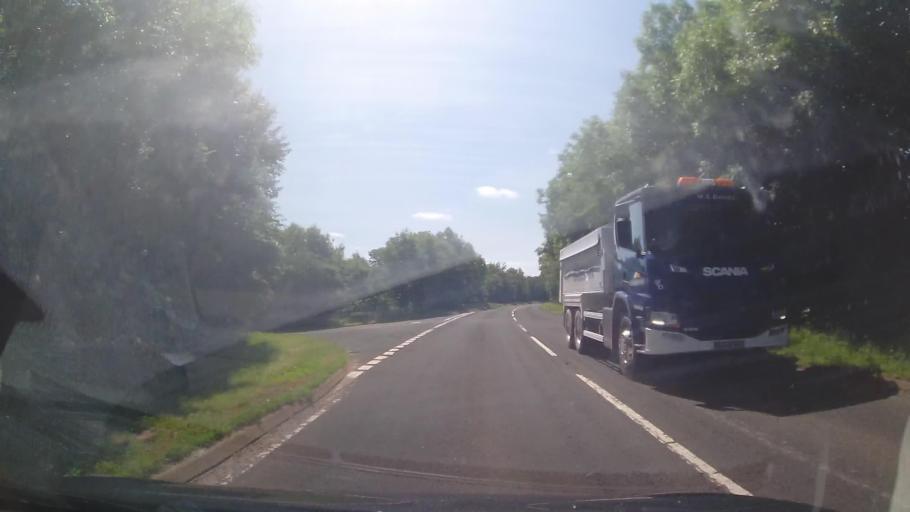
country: GB
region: England
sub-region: Herefordshire
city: Orleton
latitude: 52.3097
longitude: -2.7005
